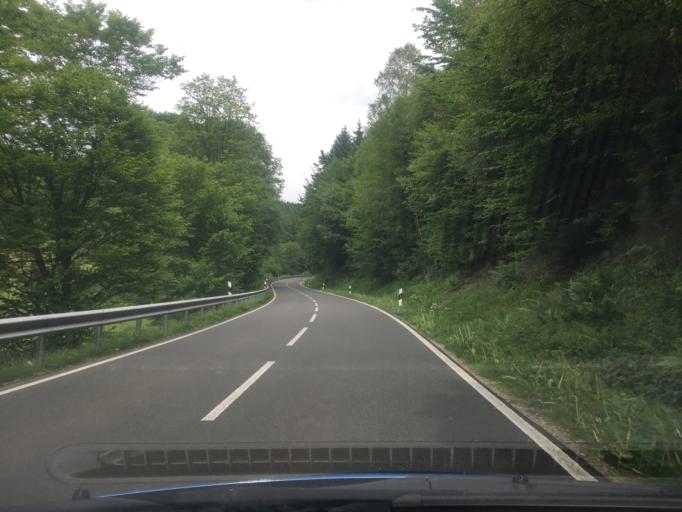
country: DE
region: Lower Saxony
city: Dassel
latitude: 51.7514
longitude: 9.6633
